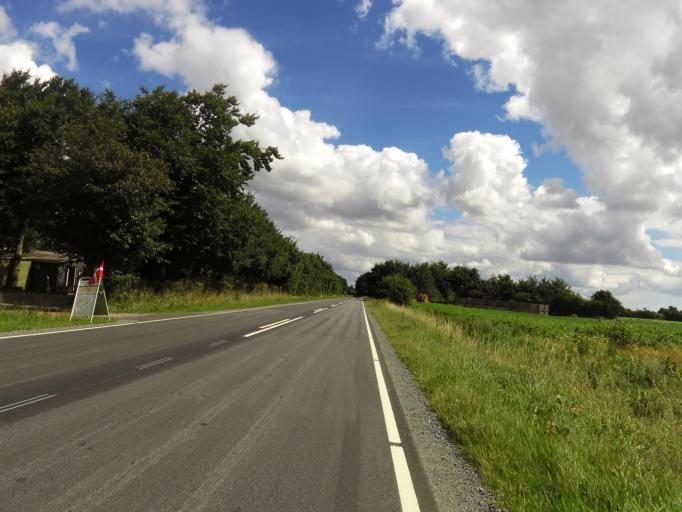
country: DK
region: South Denmark
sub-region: Haderslev Kommune
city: Vojens
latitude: 55.2802
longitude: 9.1975
